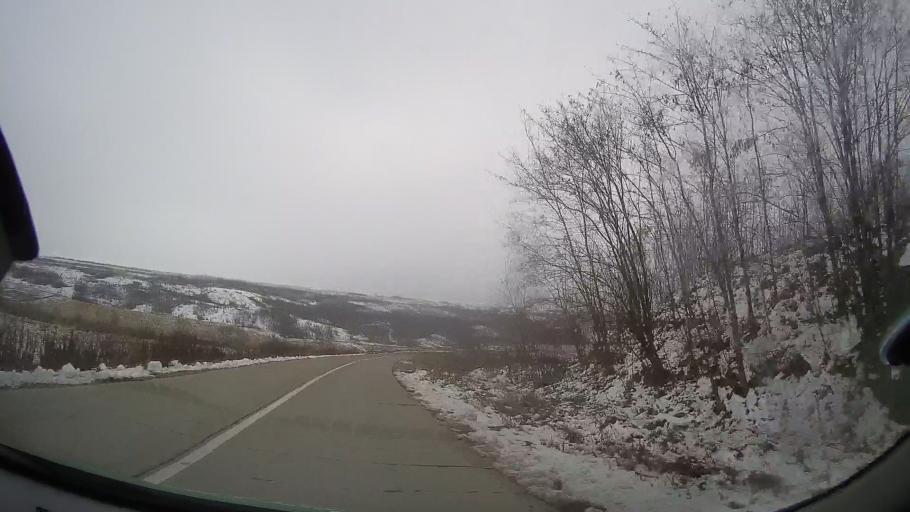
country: RO
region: Vaslui
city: Coroiesti
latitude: 46.2174
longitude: 27.4675
